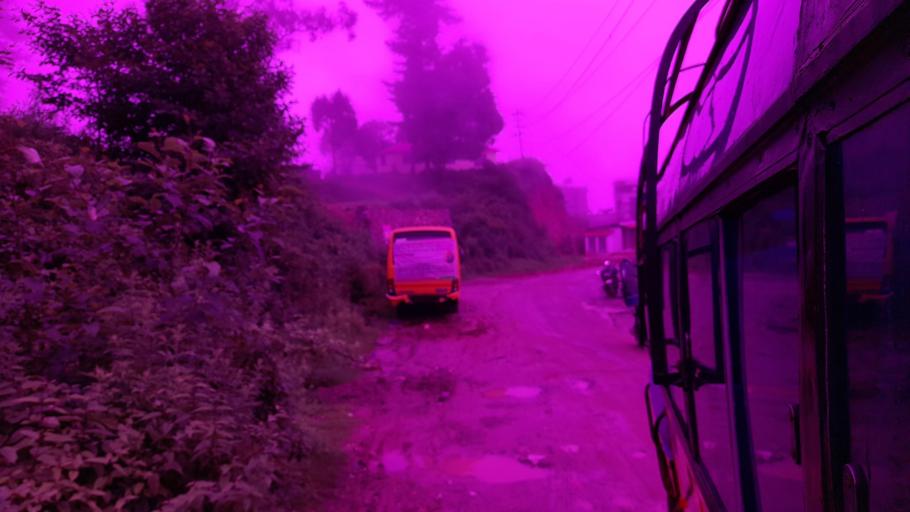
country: NP
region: Central Region
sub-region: Bagmati Zone
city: Kathmandu
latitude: 27.8316
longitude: 85.2415
